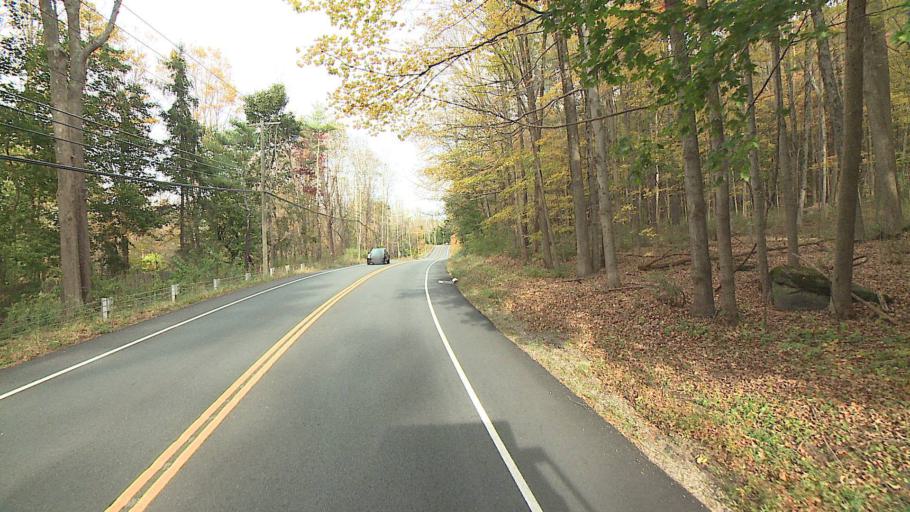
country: US
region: Connecticut
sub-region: Litchfield County
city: Canaan
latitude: 41.9935
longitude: -73.4137
